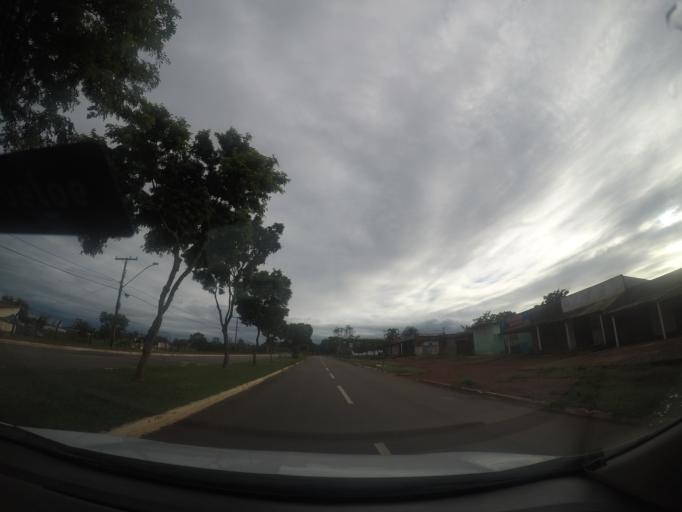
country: BR
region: Goias
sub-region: Goiania
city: Goiania
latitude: -16.6099
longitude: -49.3366
